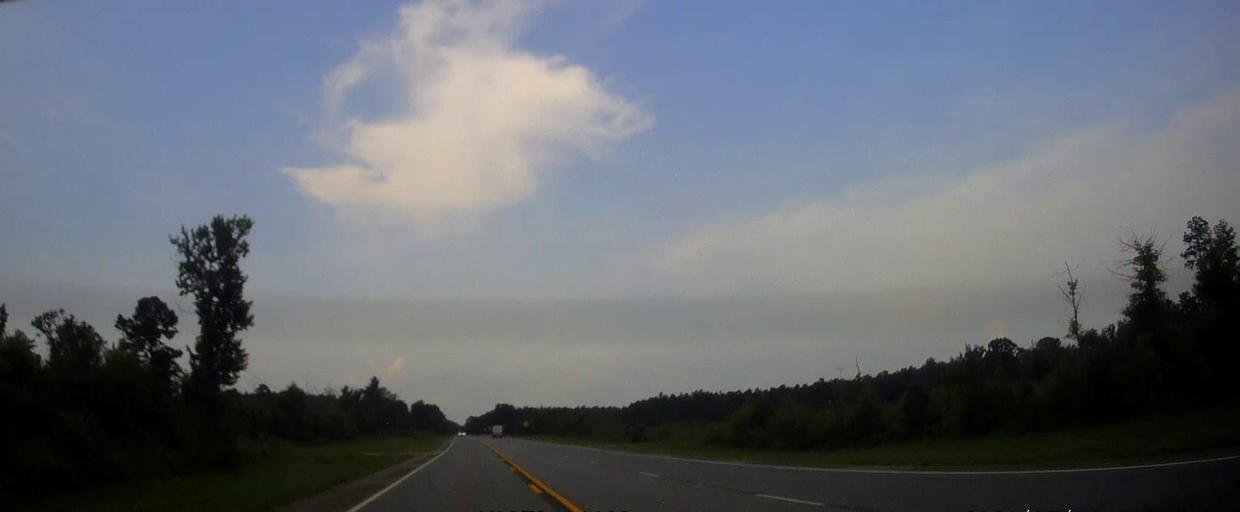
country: US
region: Georgia
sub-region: Laurens County
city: East Dublin
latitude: 32.6102
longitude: -82.8183
